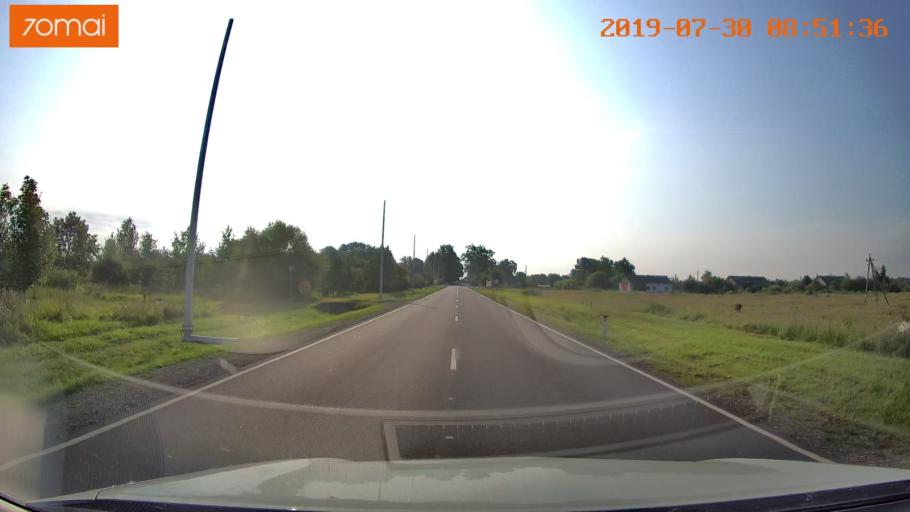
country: RU
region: Kaliningrad
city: Chernyakhovsk
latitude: 54.6018
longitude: 21.9615
